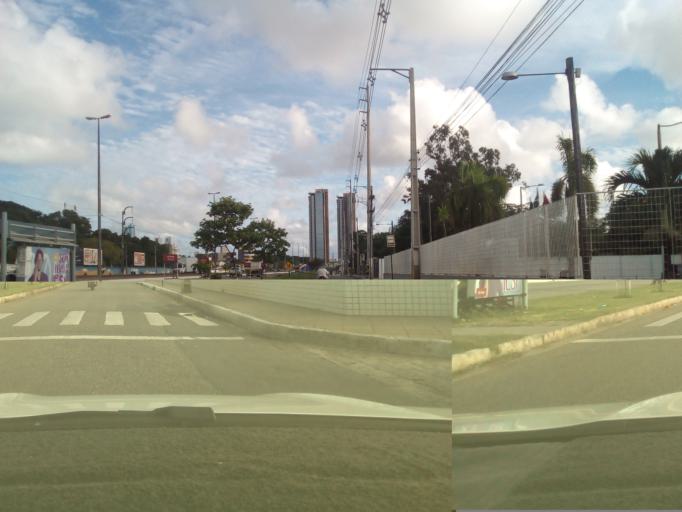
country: BR
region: Paraiba
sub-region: Joao Pessoa
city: Joao Pessoa
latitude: -7.0944
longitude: -34.8483
